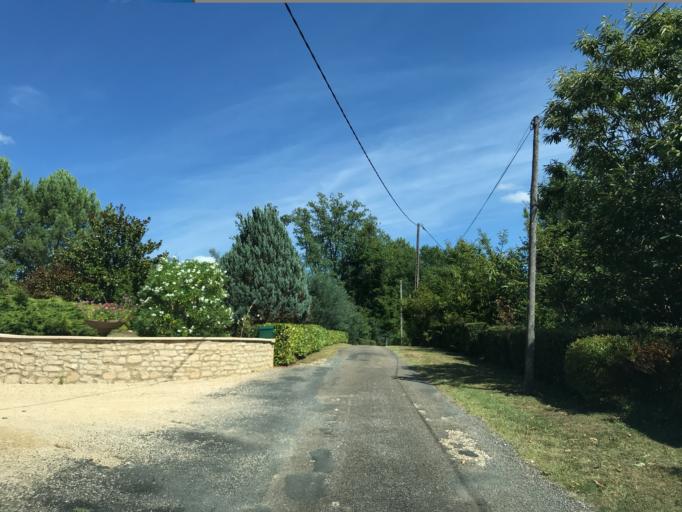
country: FR
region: Aquitaine
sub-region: Departement de la Dordogne
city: Sarlat-la-Caneda
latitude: 44.9134
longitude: 1.1729
